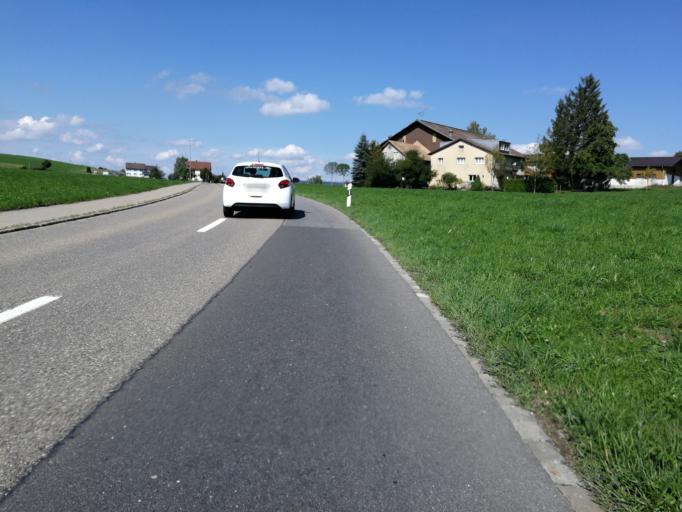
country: CH
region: Zurich
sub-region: Bezirk Horgen
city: Waedenswil / Eichweid
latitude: 47.2101
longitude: 8.6646
